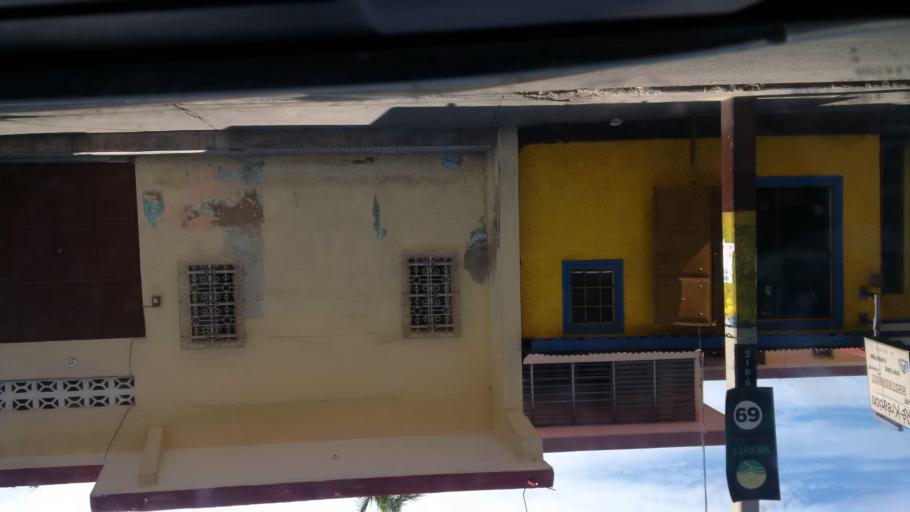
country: HT
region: Ouest
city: Port-au-Prince
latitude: 18.5360
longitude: -72.3320
